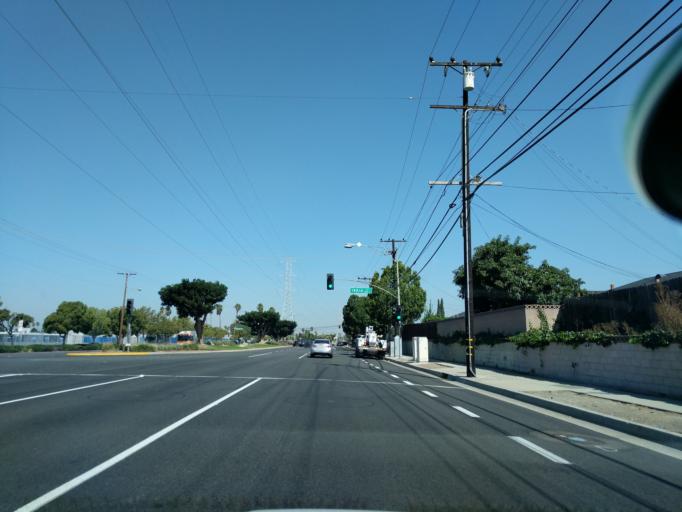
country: US
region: California
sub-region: Los Angeles County
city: Carson
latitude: 33.8566
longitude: -118.2657
